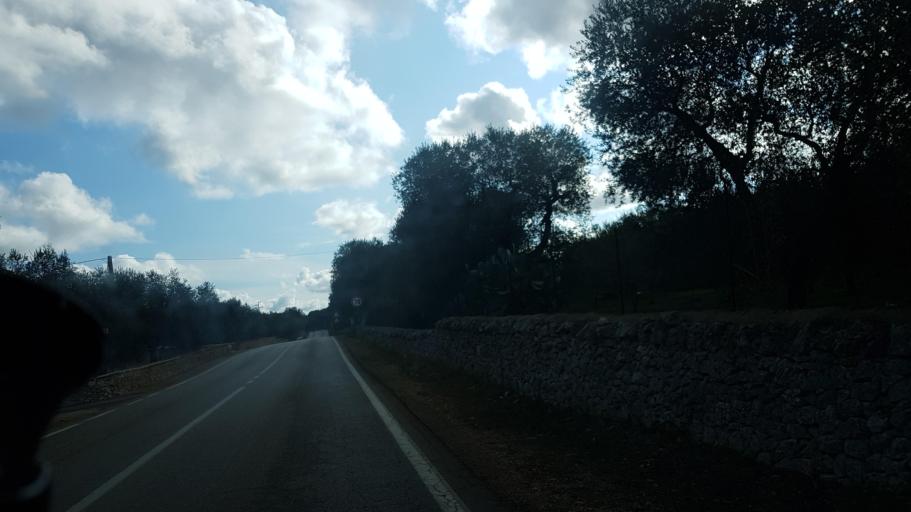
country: IT
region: Apulia
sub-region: Provincia di Brindisi
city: San Michele Salentino
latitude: 40.6606
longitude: 17.6007
